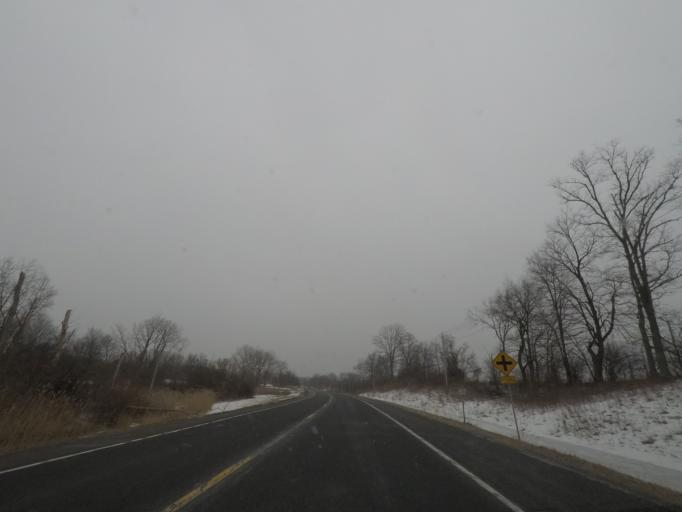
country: US
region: New York
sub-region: Albany County
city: Delmar
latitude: 42.5674
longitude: -73.8500
